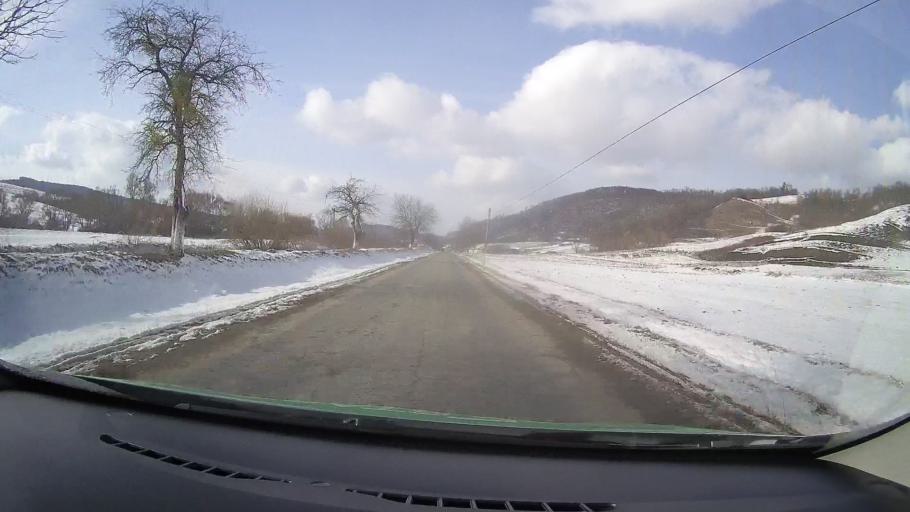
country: RO
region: Sibiu
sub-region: Comuna Iacobeni
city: Iacobeni
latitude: 46.0412
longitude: 24.7303
